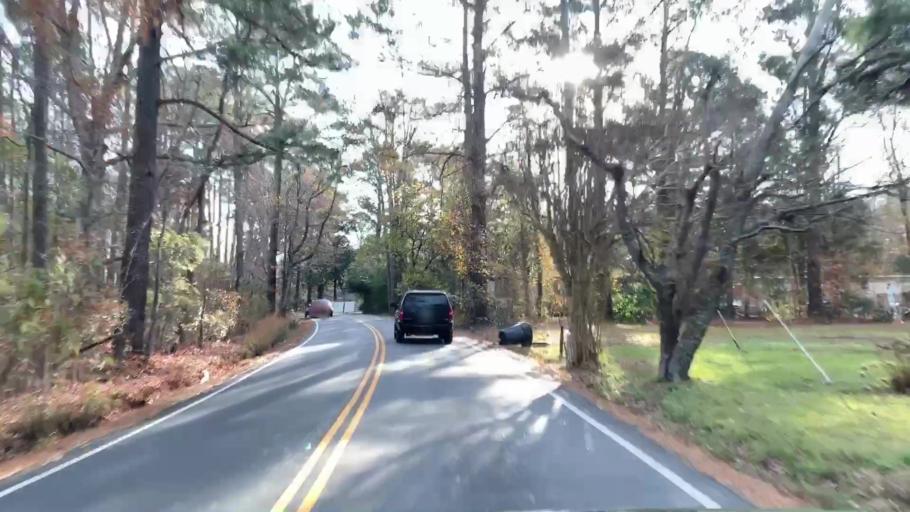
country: US
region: Virginia
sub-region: City of Virginia Beach
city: Virginia Beach
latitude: 36.6911
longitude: -76.0342
